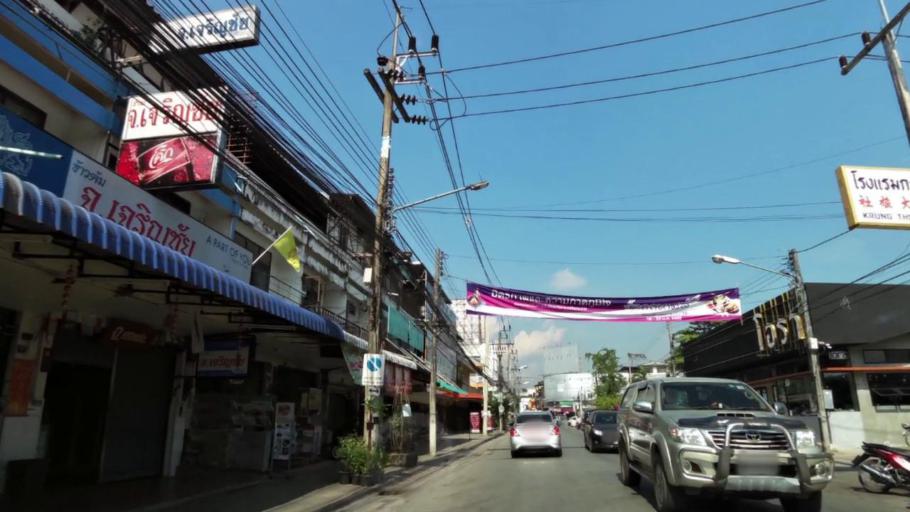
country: TH
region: Chiang Rai
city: Chiang Rai
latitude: 19.9057
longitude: 99.8285
